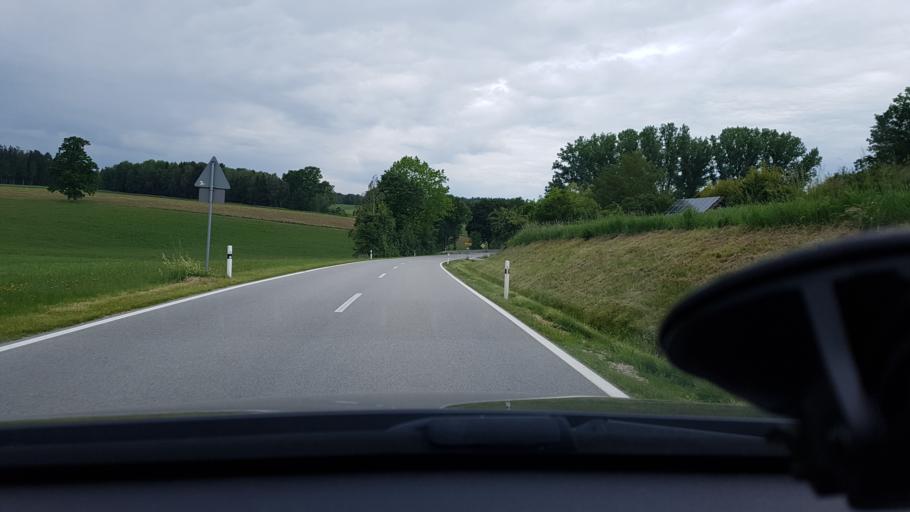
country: DE
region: Bavaria
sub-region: Lower Bavaria
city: Wittibreut
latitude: 48.3491
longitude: 13.0199
